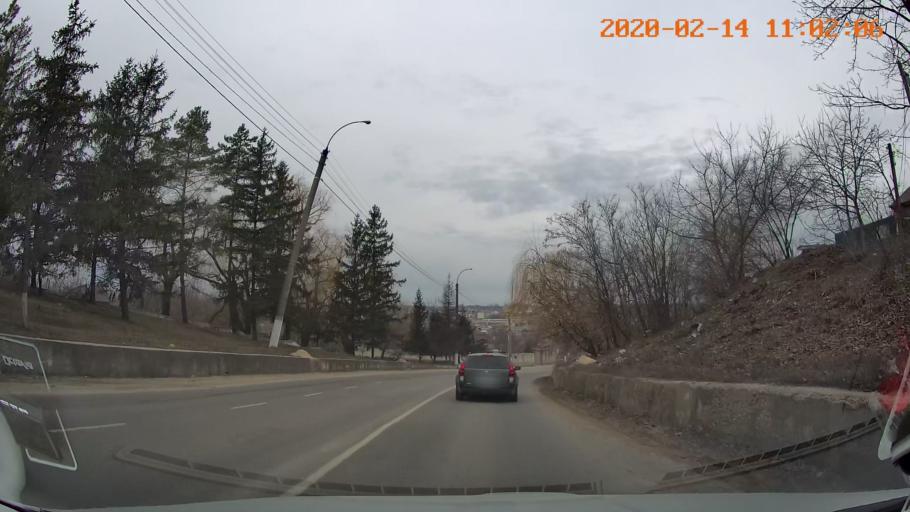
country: MD
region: Raionul Edinet
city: Edinet
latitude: 48.1629
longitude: 27.3229
